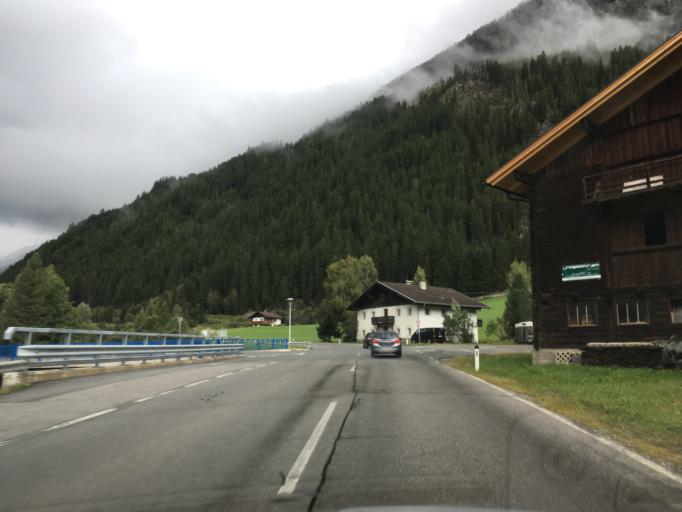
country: AT
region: Tyrol
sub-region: Politischer Bezirk Lienz
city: Innervillgraten
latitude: 46.9150
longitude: 12.3772
